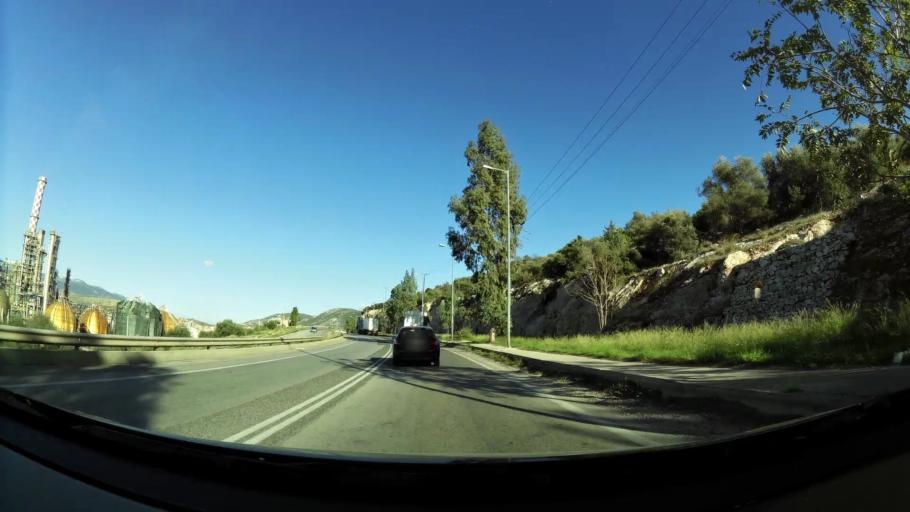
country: GR
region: Attica
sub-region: Nomarchia Athinas
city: Skaramangas
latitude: 38.0277
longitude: 23.6043
